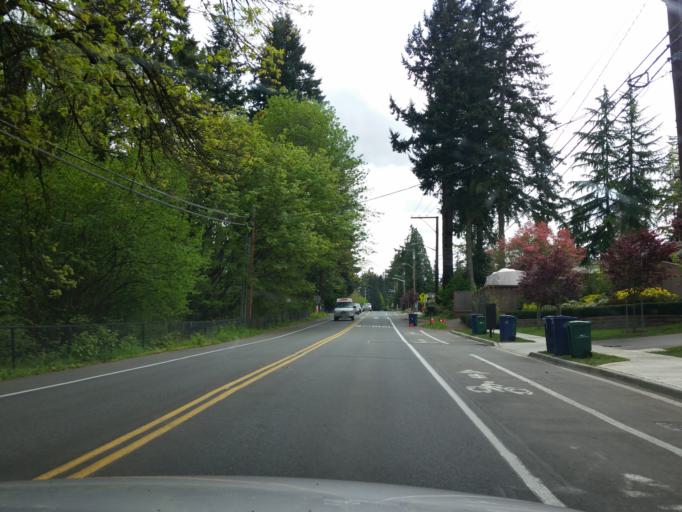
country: US
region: Washington
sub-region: King County
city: Kingsgate
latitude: 47.6871
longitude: -122.1647
